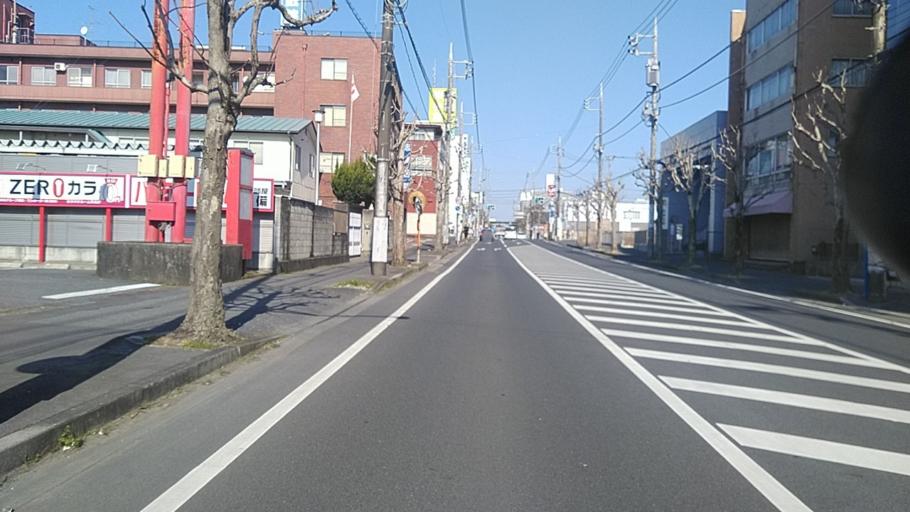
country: JP
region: Chiba
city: Mobara
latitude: 35.4231
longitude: 140.3010
